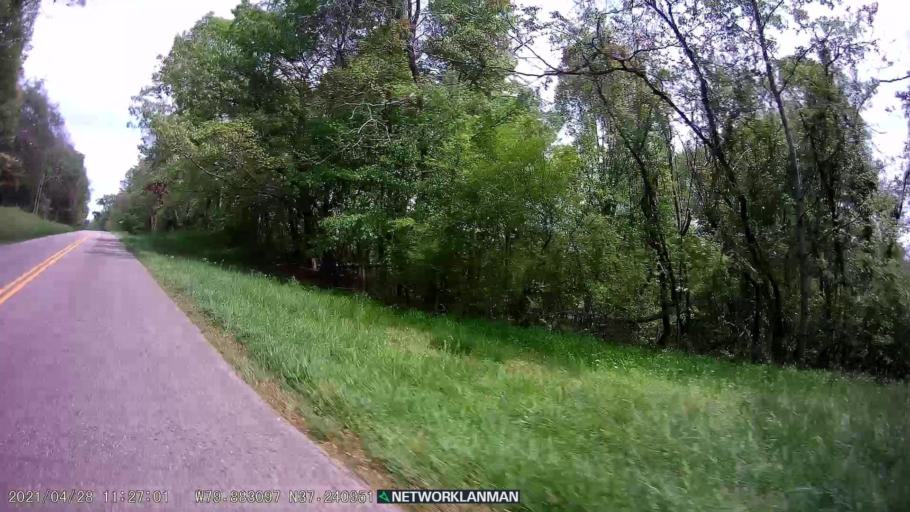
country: US
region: Virginia
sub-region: Roanoke County
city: Vinton
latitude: 37.2410
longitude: -79.8825
